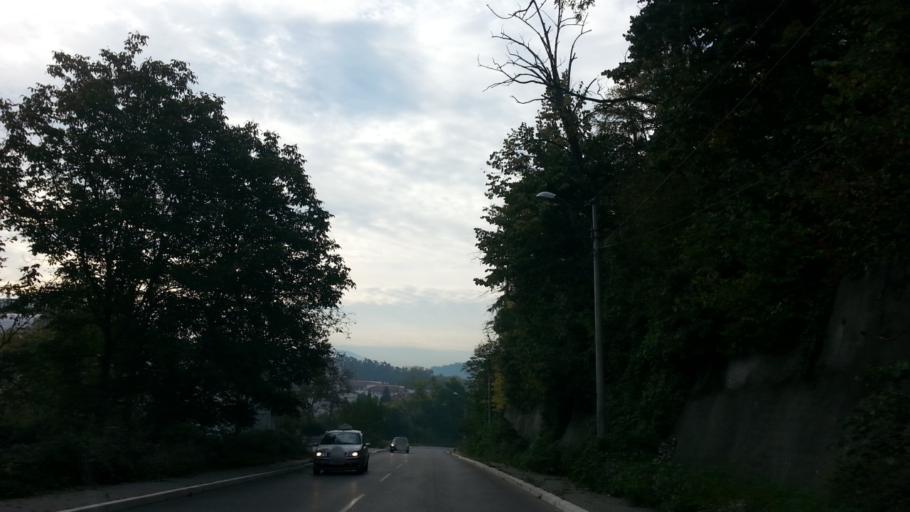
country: RS
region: Central Serbia
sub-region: Belgrade
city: Savski Venac
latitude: 44.7658
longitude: 20.4564
